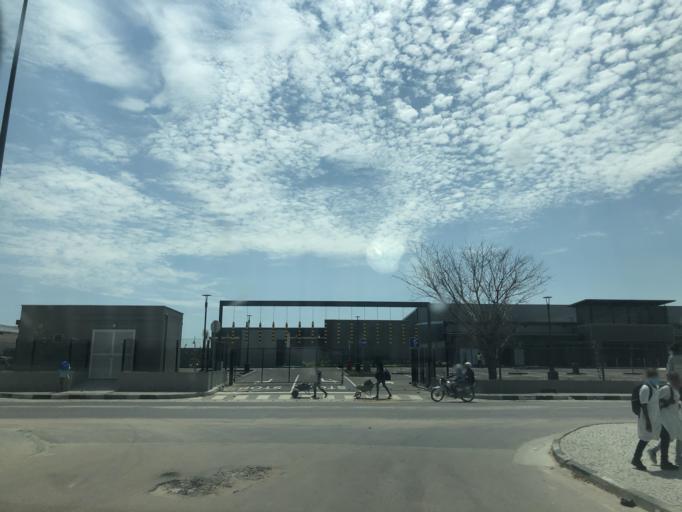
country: AO
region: Cunene
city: Ondjiva
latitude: -17.0657
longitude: 15.7288
